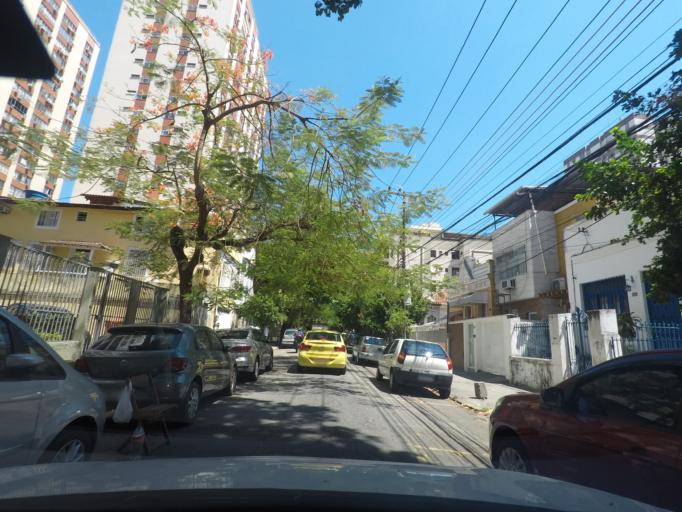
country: BR
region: Rio de Janeiro
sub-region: Rio De Janeiro
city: Rio de Janeiro
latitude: -22.9201
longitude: -43.2365
